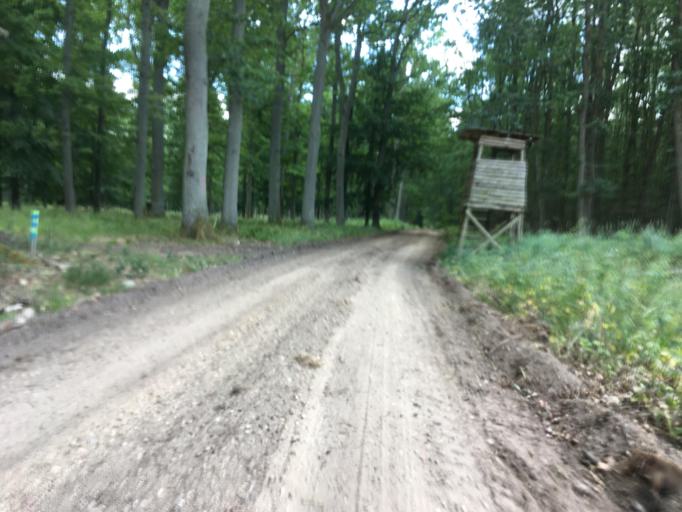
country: DE
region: Brandenburg
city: Joachimsthal
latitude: 52.9181
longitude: 13.7451
